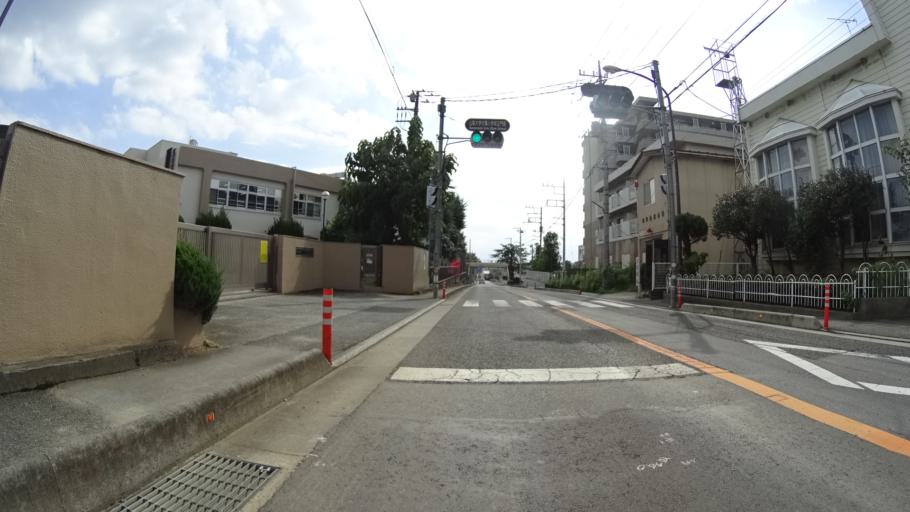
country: JP
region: Yamanashi
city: Kofu-shi
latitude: 35.6803
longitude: 138.5673
